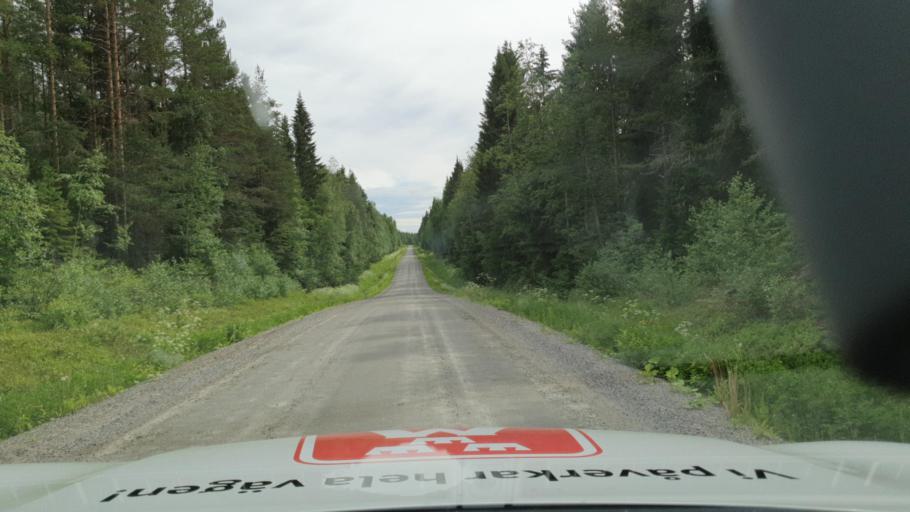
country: SE
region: Vaesterbotten
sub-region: Skelleftea Kommun
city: Burea
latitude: 64.4345
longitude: 21.0155
